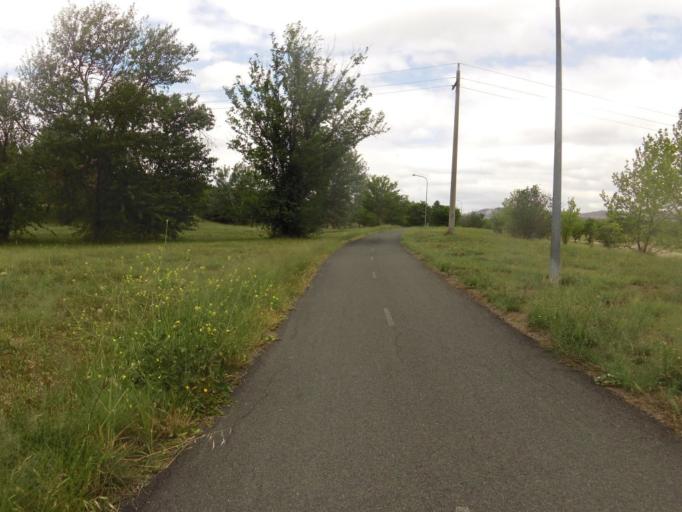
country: AU
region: Australian Capital Territory
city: Macarthur
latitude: -35.4219
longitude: 149.0982
